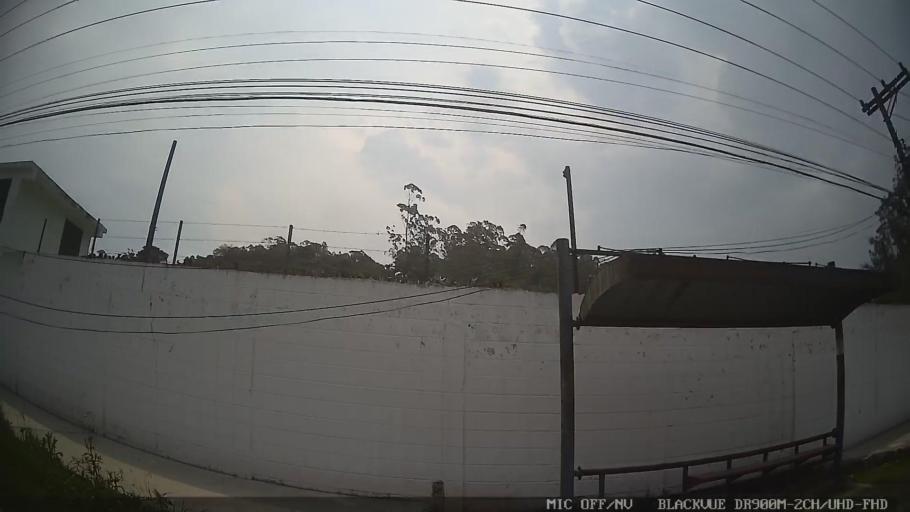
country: BR
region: Sao Paulo
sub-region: Ribeirao Pires
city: Ribeirao Pires
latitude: -23.6875
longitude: -46.3922
